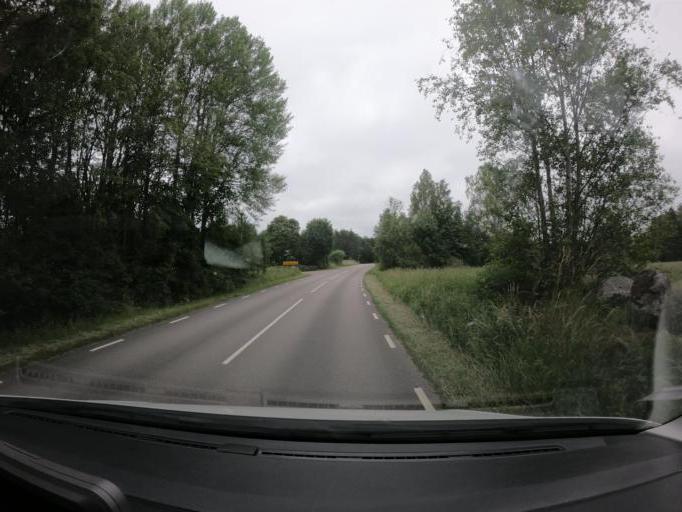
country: SE
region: Skane
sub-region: Perstorps Kommun
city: Perstorp
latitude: 56.0871
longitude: 13.3986
